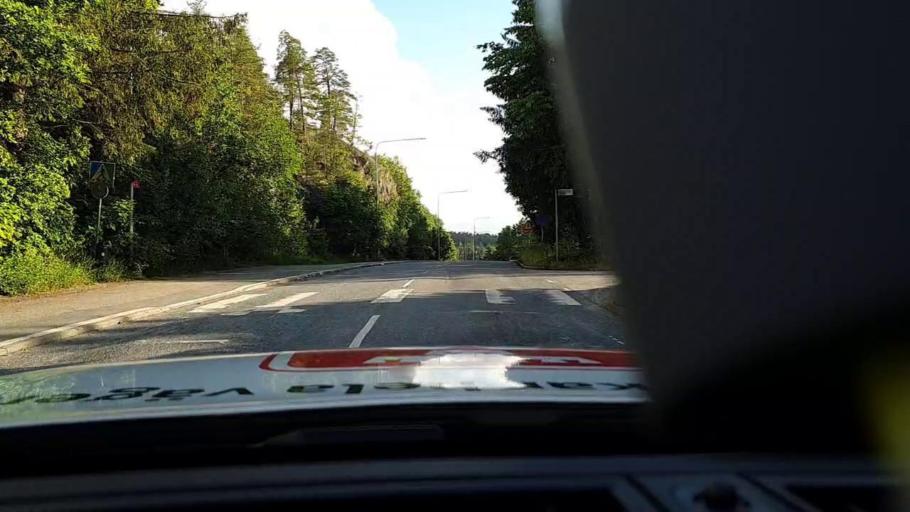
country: SE
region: Stockholm
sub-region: Huddinge Kommun
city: Huddinge
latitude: 59.2526
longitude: 17.9686
